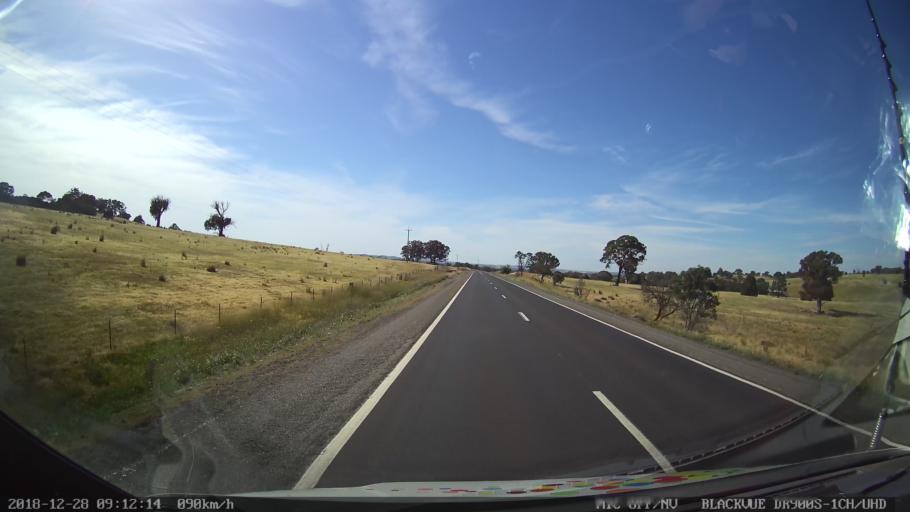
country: AU
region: New South Wales
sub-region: Upper Lachlan Shire
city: Crookwell
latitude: -34.2530
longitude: 149.3402
